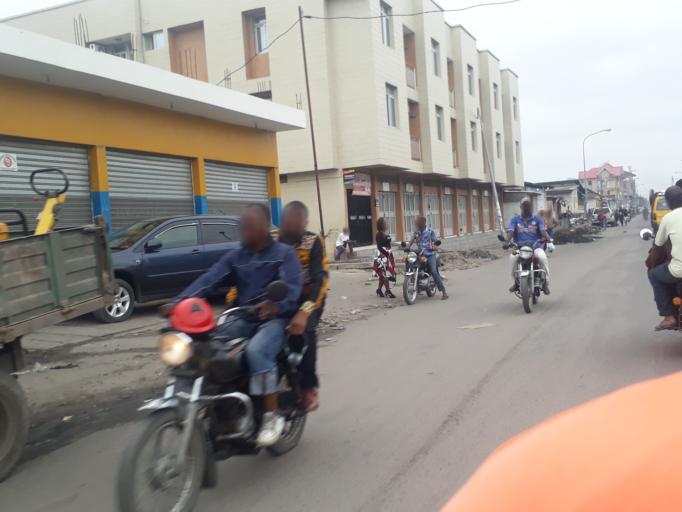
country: CD
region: Kinshasa
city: Kinshasa
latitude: -4.3172
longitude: 15.3105
